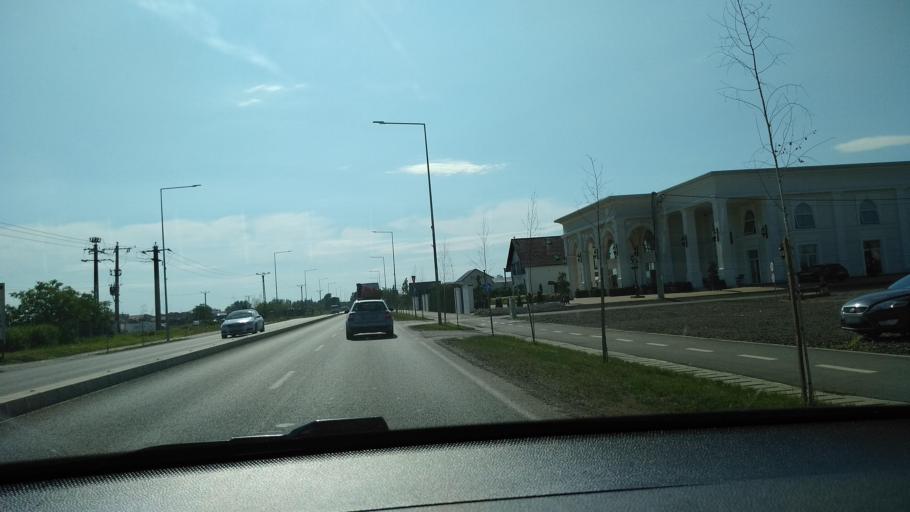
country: RO
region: Timis
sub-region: Comuna Mosnita Noua
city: Mosnita Noua
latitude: 45.7224
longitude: 21.3028
